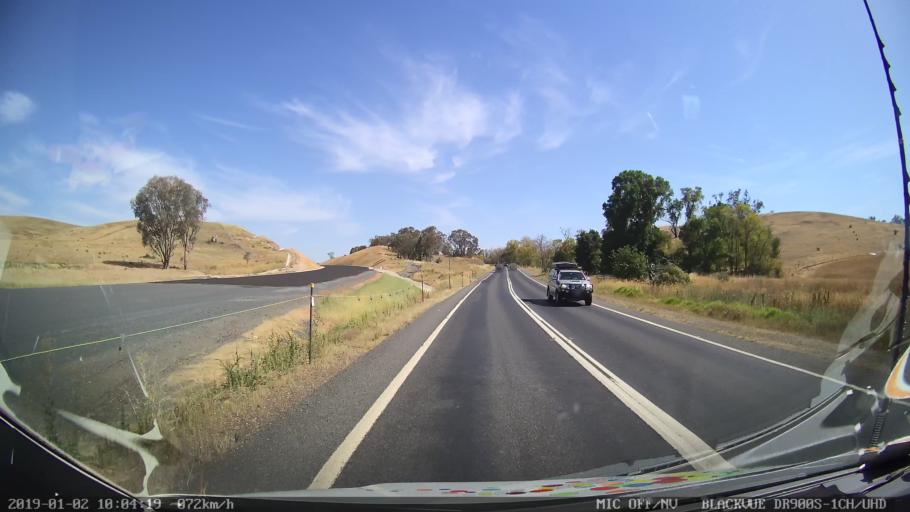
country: AU
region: New South Wales
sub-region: Gundagai
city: Gundagai
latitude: -35.1689
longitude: 148.1233
